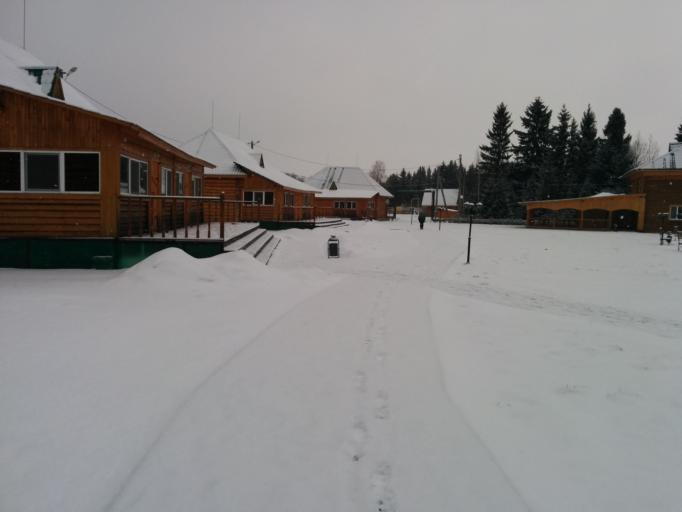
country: RU
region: Perm
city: Osa
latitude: 57.4605
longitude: 55.4685
